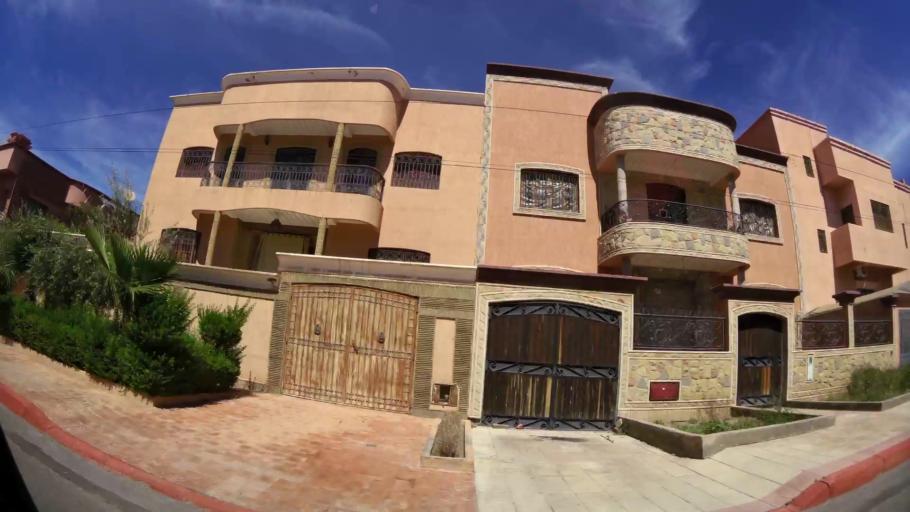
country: MA
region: Marrakech-Tensift-Al Haouz
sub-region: Marrakech
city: Marrakesh
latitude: 31.6660
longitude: -8.0077
